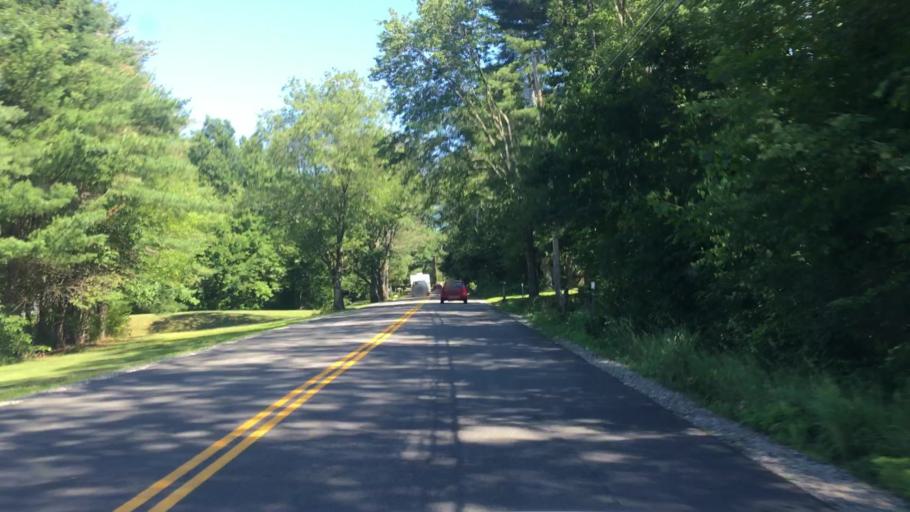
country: US
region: New Hampshire
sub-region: Rockingham County
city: Auburn
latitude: 43.0264
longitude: -71.3795
